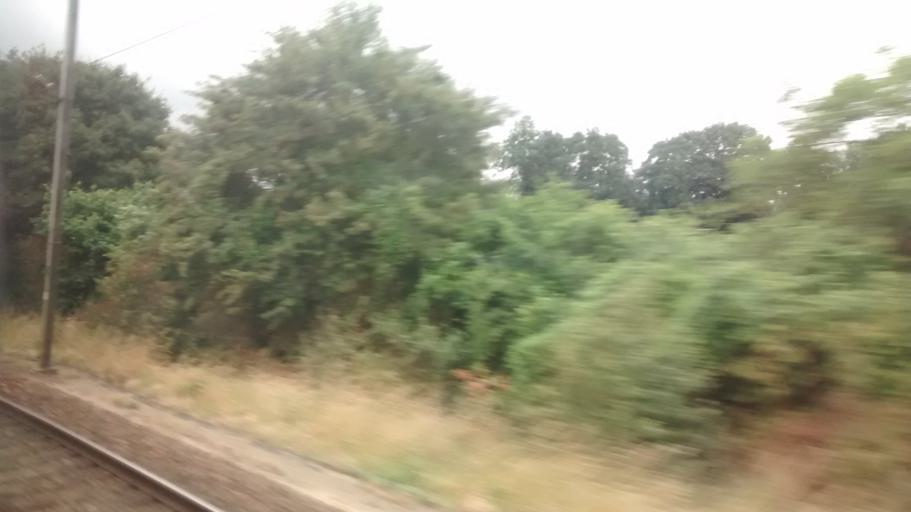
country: FR
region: Pays de la Loire
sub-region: Departement de la Mayenne
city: Louverne
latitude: 48.1114
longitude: -0.7095
